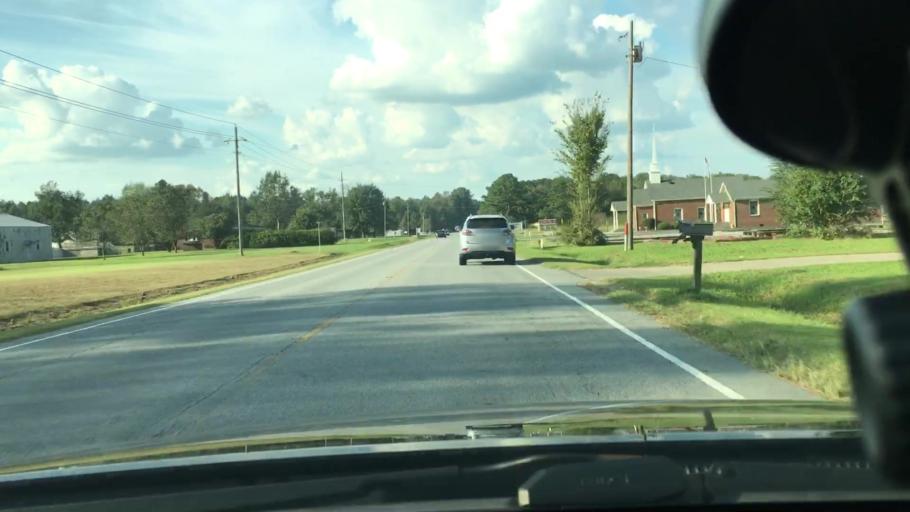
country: US
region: North Carolina
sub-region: Pitt County
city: Windsor
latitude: 35.4303
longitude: -77.2620
